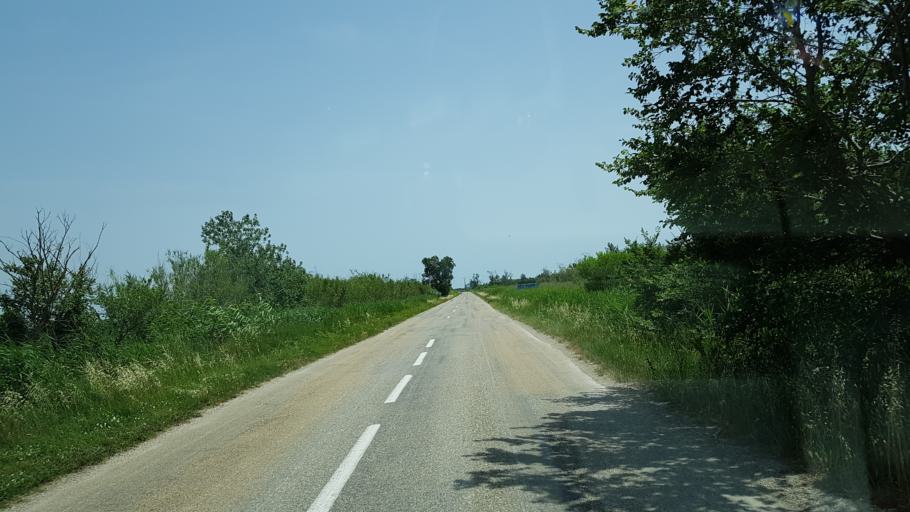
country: FR
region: Provence-Alpes-Cote d'Azur
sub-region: Departement des Bouches-du-Rhone
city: Port-Saint-Louis-du-Rhone
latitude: 43.4472
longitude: 4.6624
